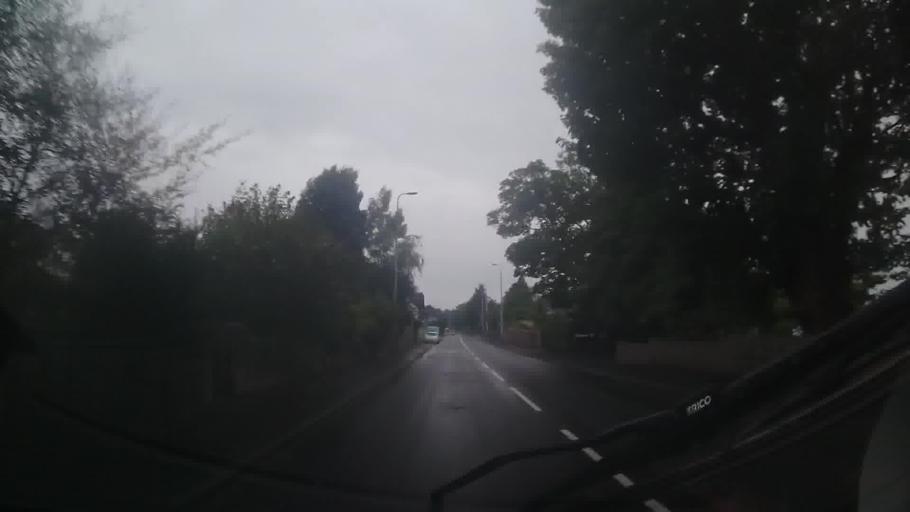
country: GB
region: Scotland
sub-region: North Ayrshire
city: Fairlie
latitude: 55.7548
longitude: -4.8544
